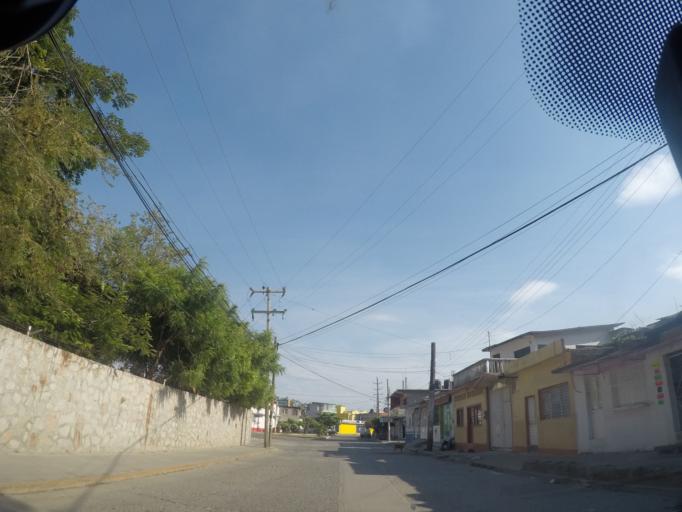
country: MX
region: Oaxaca
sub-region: Salina Cruz
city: Salina Cruz
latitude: 16.1744
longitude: -95.1977
